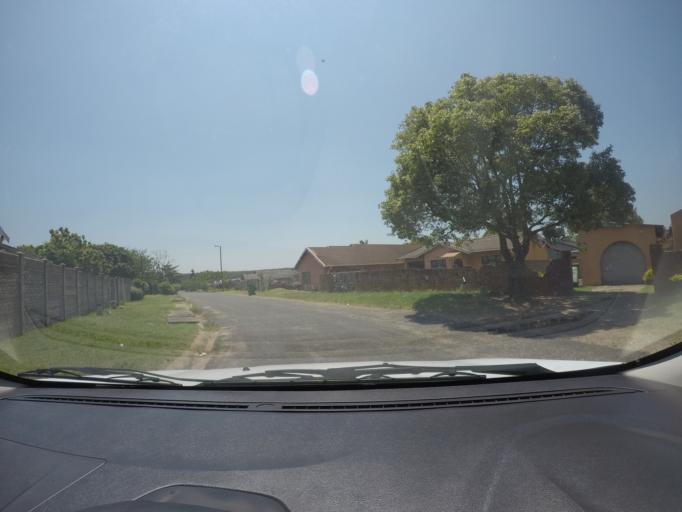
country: ZA
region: KwaZulu-Natal
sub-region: uThungulu District Municipality
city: eSikhawini
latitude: -28.8912
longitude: 31.8838
